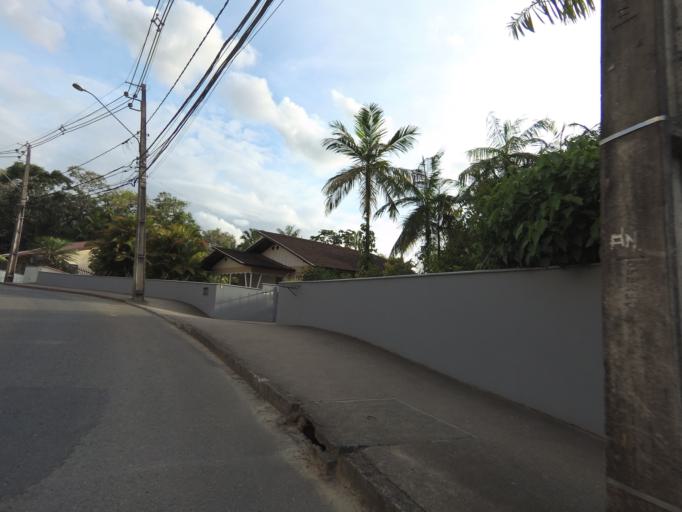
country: BR
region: Santa Catarina
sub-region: Blumenau
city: Blumenau
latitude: -26.9068
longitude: -49.1231
